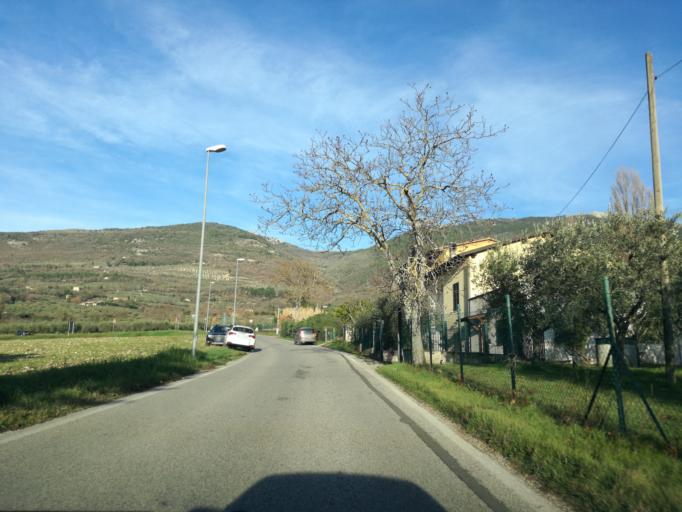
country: IT
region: Umbria
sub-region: Provincia di Perugia
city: Rivotorto
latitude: 43.0466
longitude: 12.6265
